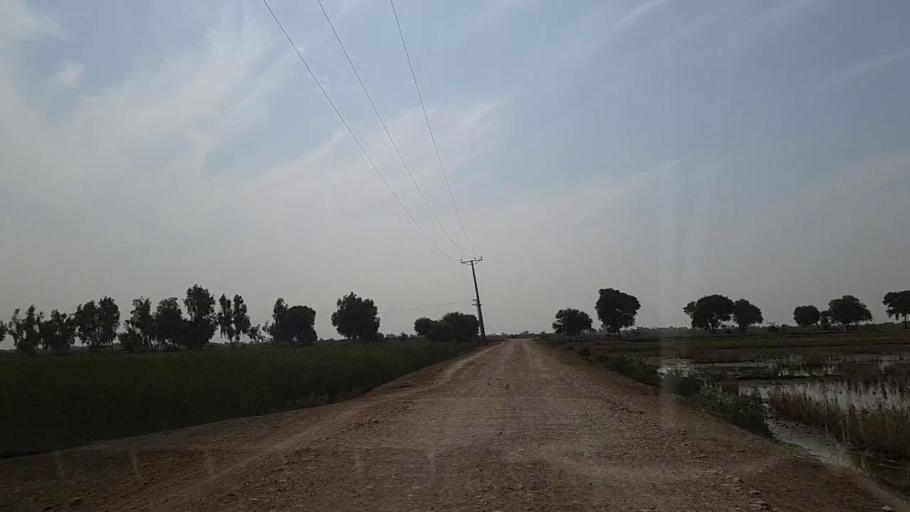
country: PK
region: Sindh
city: Mirpur Batoro
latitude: 24.6125
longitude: 68.2364
